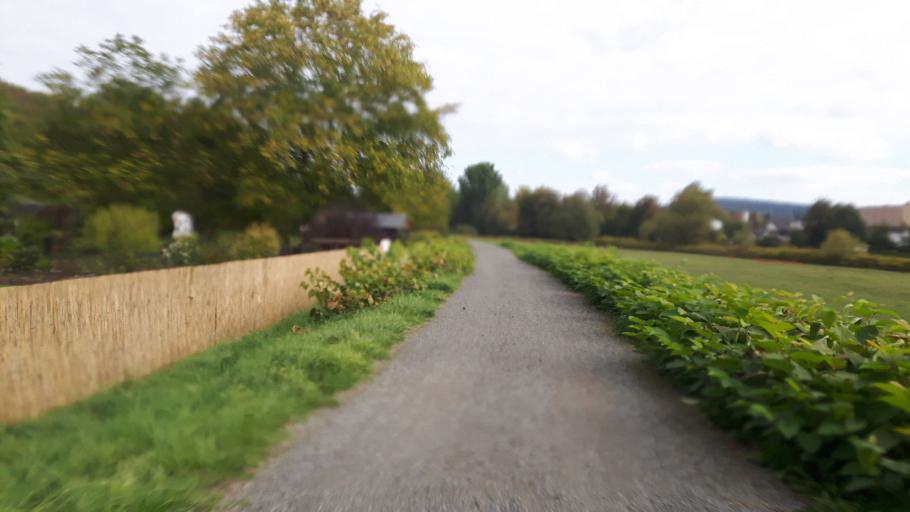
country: DE
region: North Rhine-Westphalia
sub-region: Regierungsbezirk Koln
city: Eitorf
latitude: 50.7785
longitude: 7.4383
